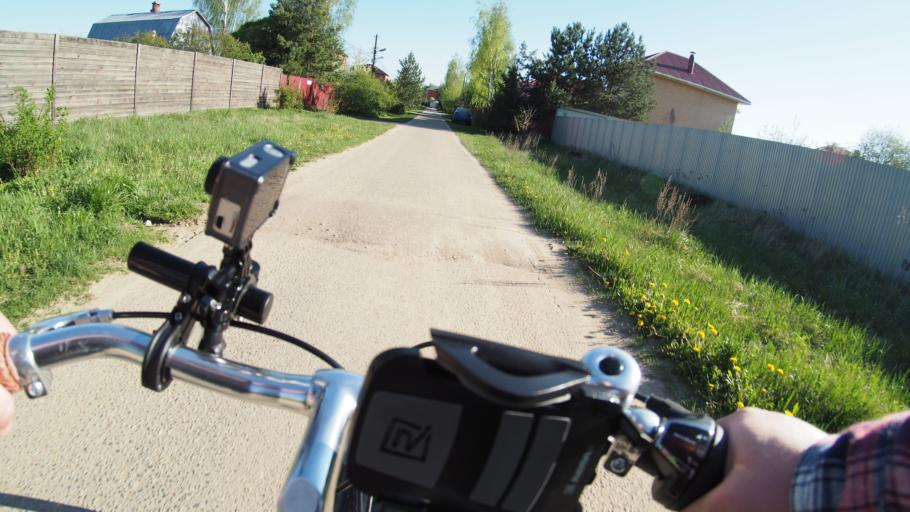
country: RU
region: Moskovskaya
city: Ramenskoye
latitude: 55.5498
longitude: 38.1936
